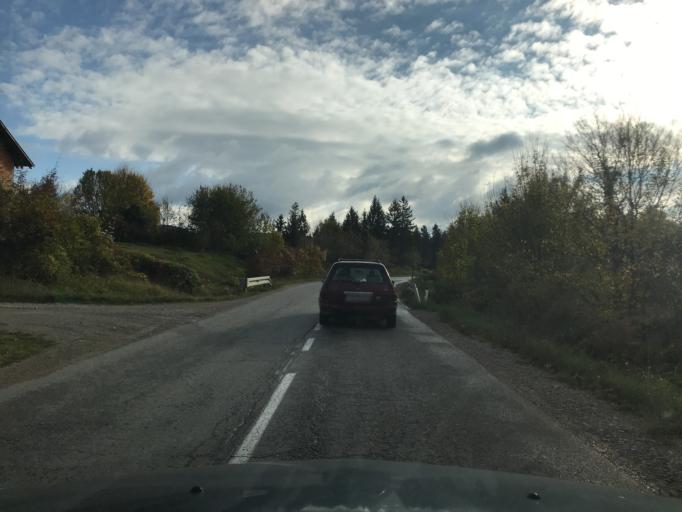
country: BA
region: Republika Srpska
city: Skender Vakuf
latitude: 44.4998
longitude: 17.3594
